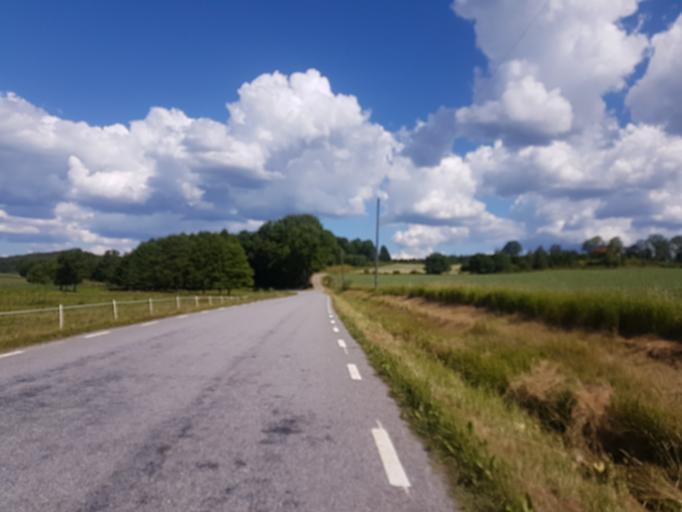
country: SE
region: Soedermanland
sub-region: Gnesta Kommun
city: Gnesta
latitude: 59.0654
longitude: 17.3329
